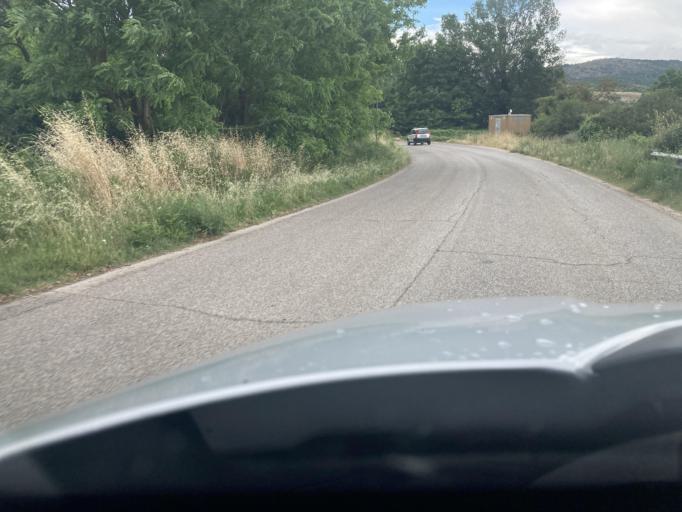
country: IT
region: Abruzzo
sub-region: Provincia dell' Aquila
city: Sant'Eusanio Forconese
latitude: 42.2924
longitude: 13.5282
